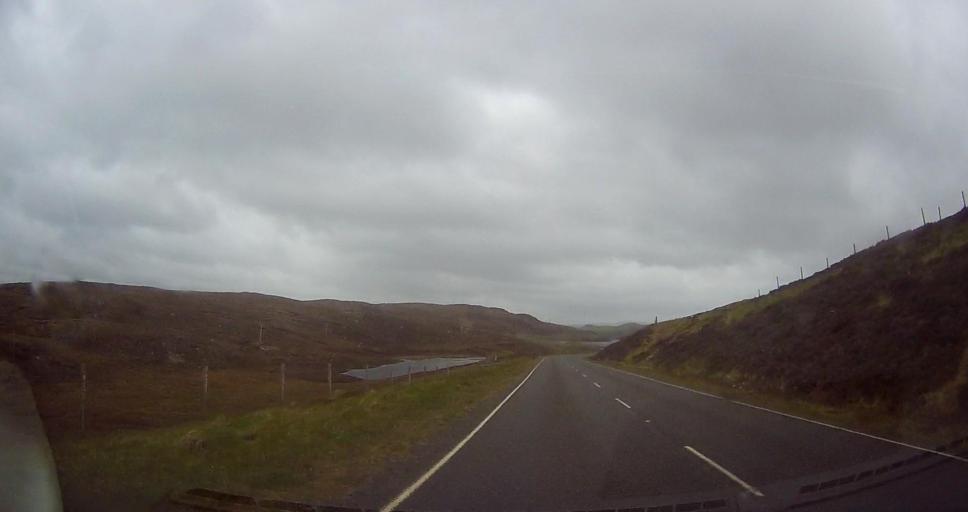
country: GB
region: Scotland
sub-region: Shetland Islands
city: Lerwick
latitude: 60.4499
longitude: -1.3958
